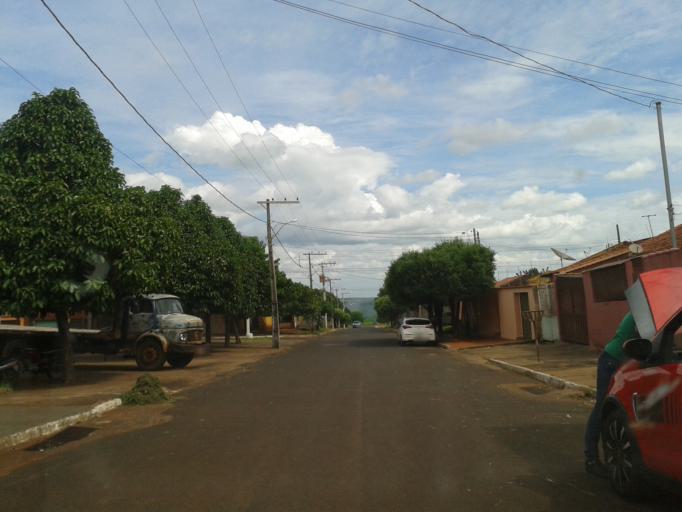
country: BR
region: Goias
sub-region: Itumbiara
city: Itumbiara
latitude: -18.4311
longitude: -49.1902
